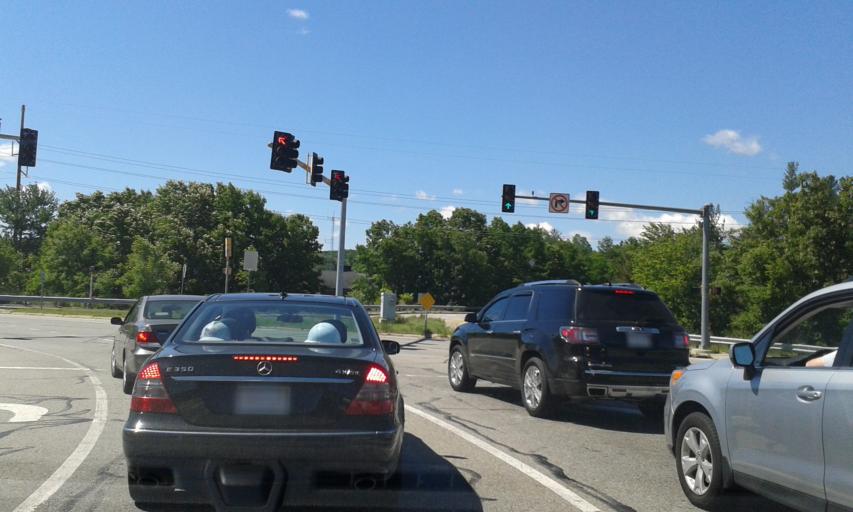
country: US
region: Massachusetts
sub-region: Middlesex County
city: Chelmsford
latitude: 42.6222
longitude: -71.3672
